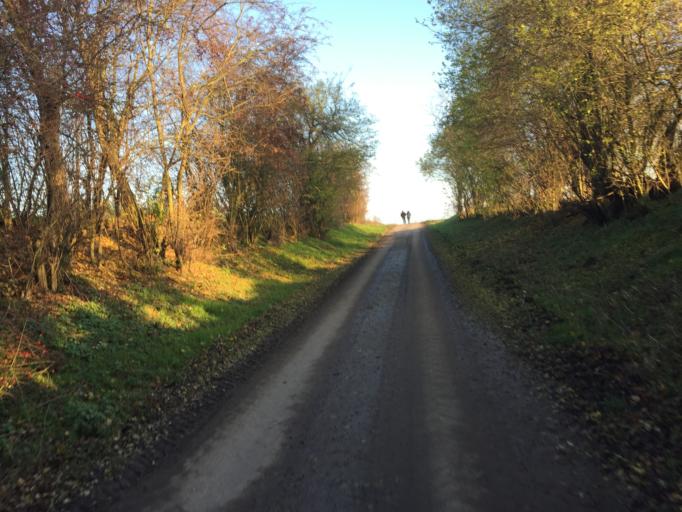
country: DE
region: Hesse
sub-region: Regierungsbezirk Darmstadt
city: Munzenberg
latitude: 50.4856
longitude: 8.7339
